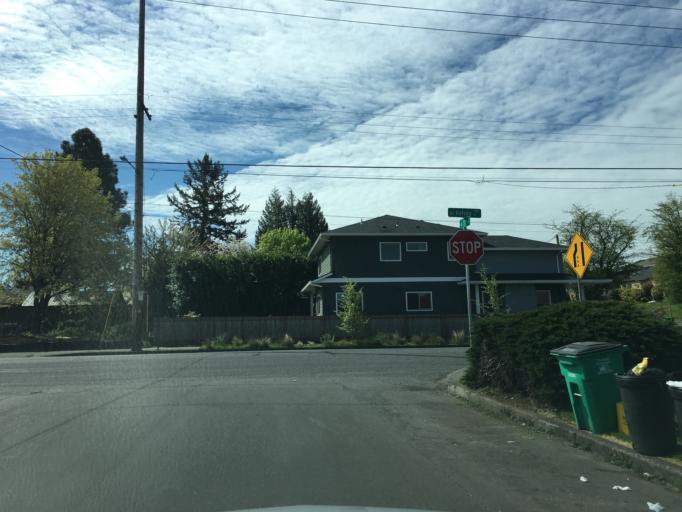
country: US
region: Oregon
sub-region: Multnomah County
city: Lents
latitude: 45.5338
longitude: -122.5894
